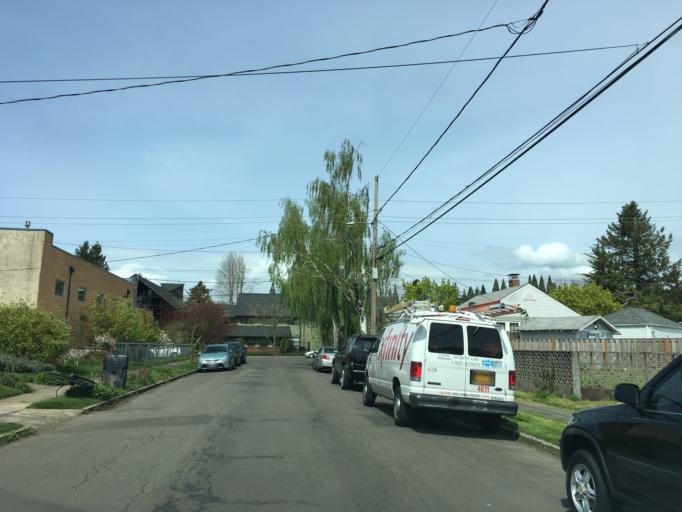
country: US
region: Oregon
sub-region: Multnomah County
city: Lents
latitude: 45.5474
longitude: -122.5778
